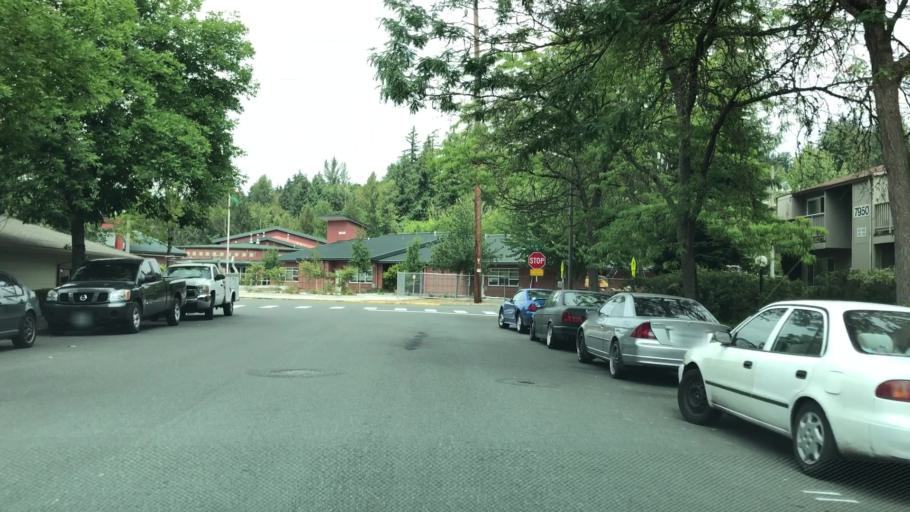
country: US
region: Washington
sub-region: King County
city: Redmond
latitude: 47.6742
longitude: -122.1163
